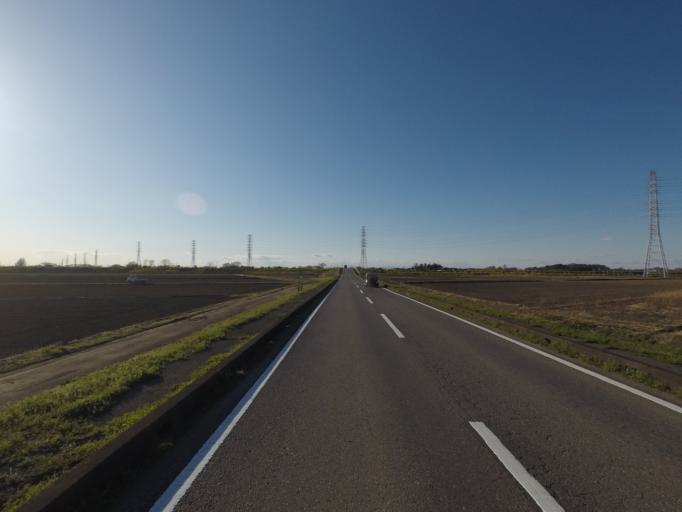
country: JP
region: Ibaraki
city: Ishige
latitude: 36.1733
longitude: 140.0142
